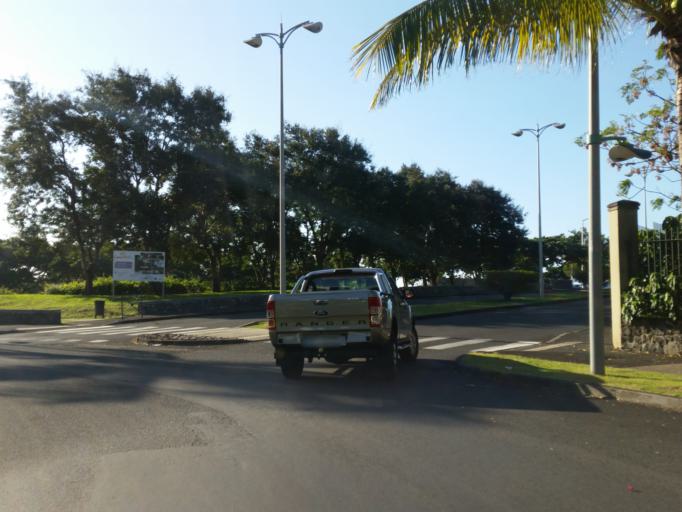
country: RE
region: Reunion
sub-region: Reunion
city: Saint-Denis
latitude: -20.8945
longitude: 55.4701
